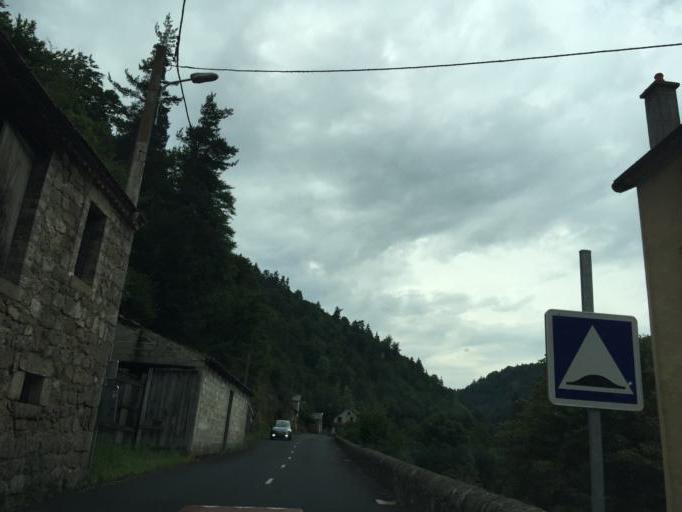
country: FR
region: Languedoc-Roussillon
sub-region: Departement de la Lozere
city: Langogne
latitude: 44.8366
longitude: 3.7374
